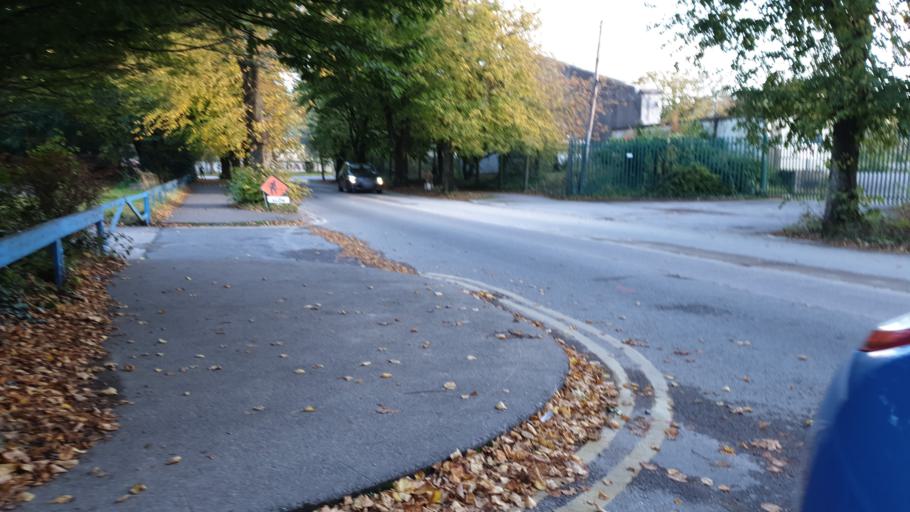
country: IE
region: Munster
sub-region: County Cork
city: Cork
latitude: 51.8986
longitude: -8.4424
